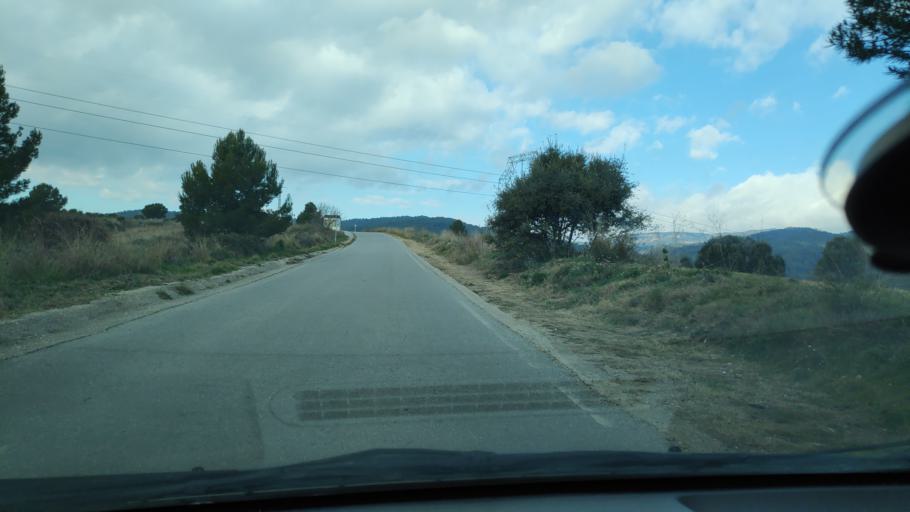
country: ES
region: Catalonia
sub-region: Provincia de Barcelona
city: Terrassa
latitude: 41.5757
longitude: 1.9871
